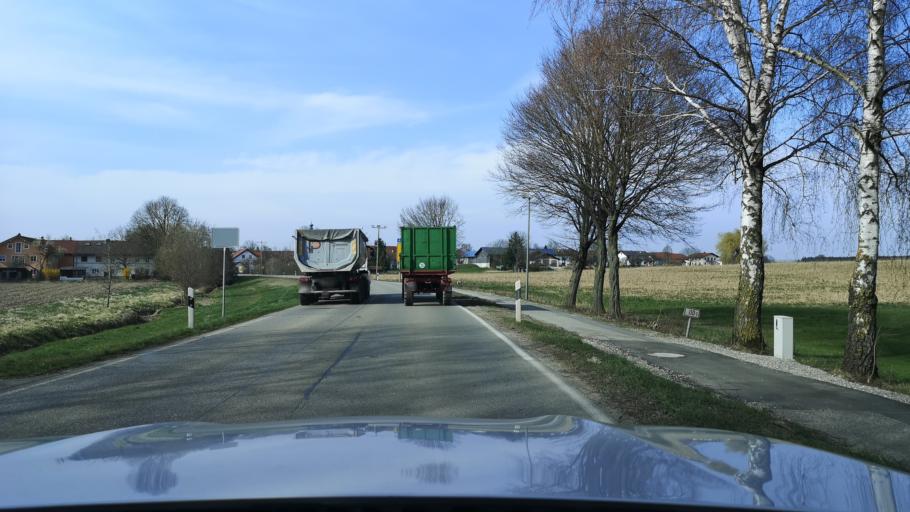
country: DE
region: Bavaria
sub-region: Upper Bavaria
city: Pastetten
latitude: 48.2038
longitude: 11.9620
